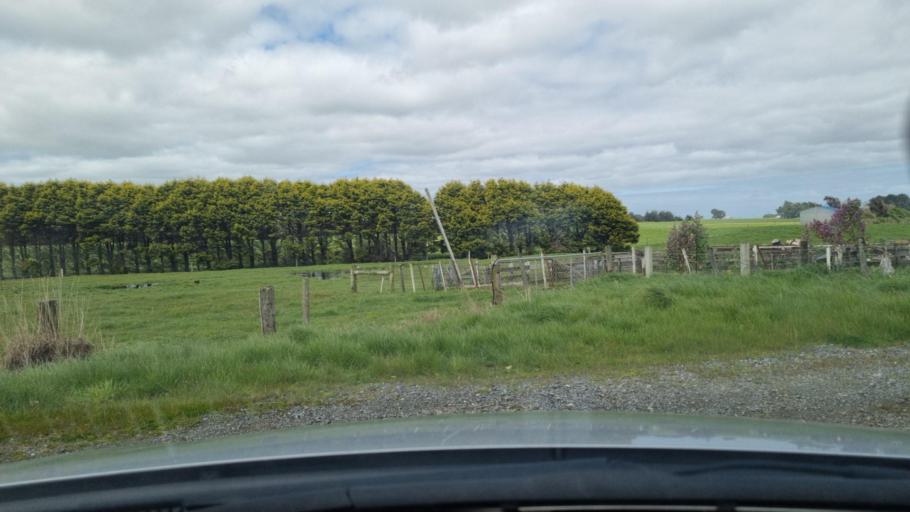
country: NZ
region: Southland
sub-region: Invercargill City
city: Invercargill
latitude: -46.4343
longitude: 168.4142
